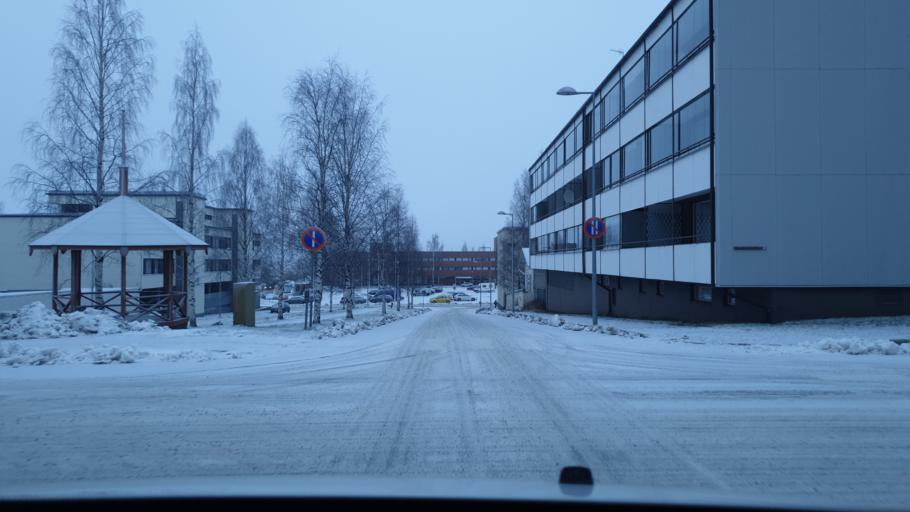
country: FI
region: Lapland
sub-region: Kemi-Tornio
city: Kemi
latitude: 65.7339
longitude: 24.5618
